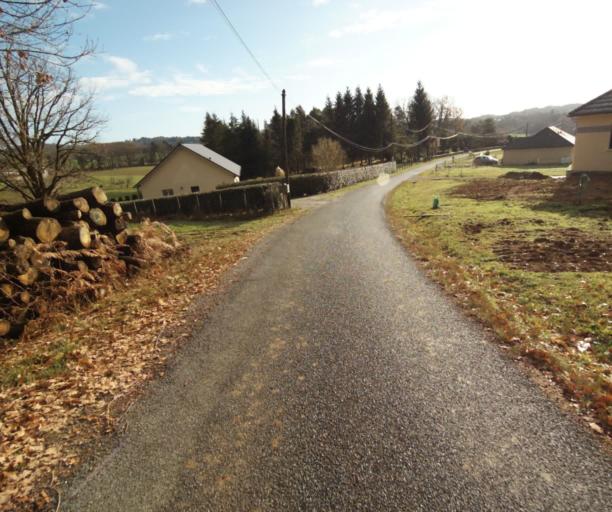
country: FR
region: Limousin
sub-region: Departement de la Correze
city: Saint-Mexant
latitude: 45.2754
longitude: 1.6088
